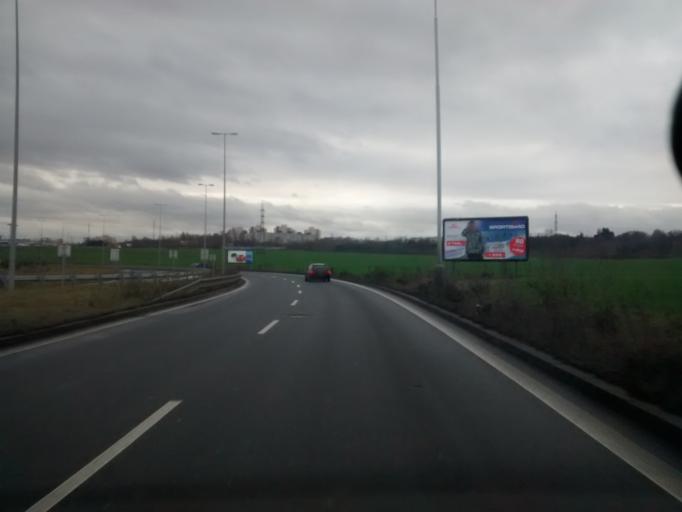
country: CZ
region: Praha
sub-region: Praha 9
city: Strizkov
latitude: 50.1404
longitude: 14.4933
